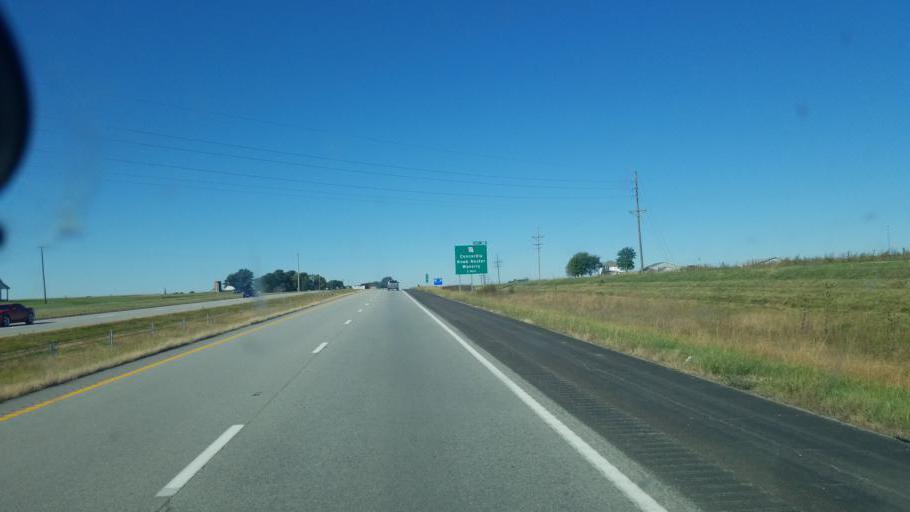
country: US
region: Missouri
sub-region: Lafayette County
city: Concordia
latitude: 38.9891
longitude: -93.5456
